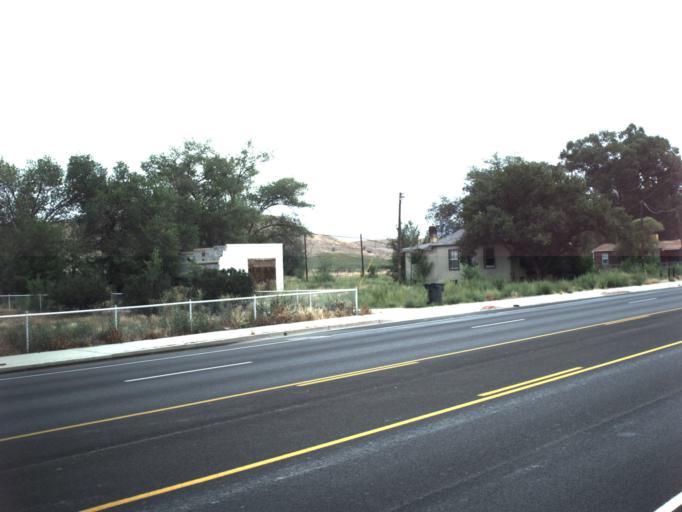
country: US
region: Utah
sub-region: Carbon County
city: Wellington
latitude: 39.5424
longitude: -110.7306
